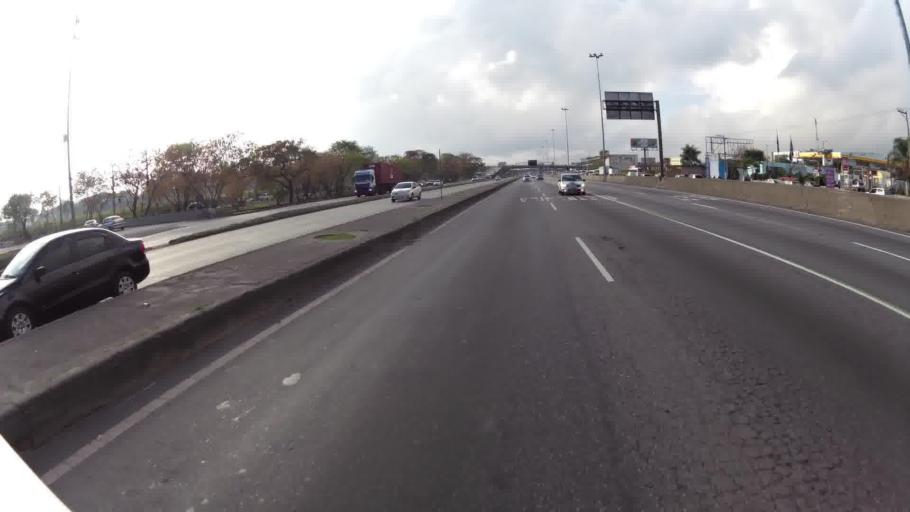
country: BR
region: Rio de Janeiro
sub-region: Duque De Caxias
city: Duque de Caxias
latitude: -22.8230
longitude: -43.2794
